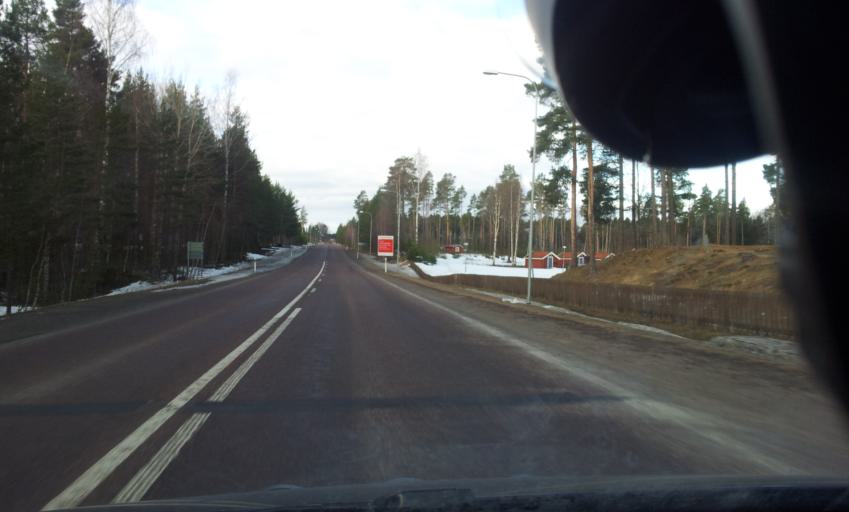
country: SE
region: Gaevleborg
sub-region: Ljusdals Kommun
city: Ljusdal
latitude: 61.8388
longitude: 16.0415
